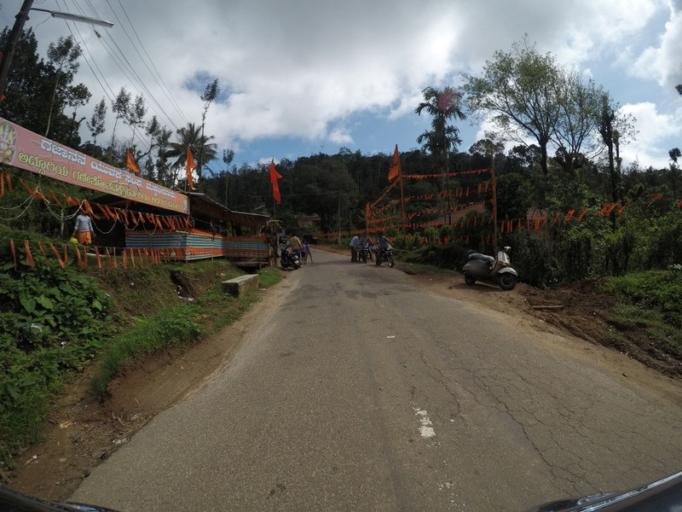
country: IN
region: Karnataka
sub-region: Kodagu
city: Madikeri
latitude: 12.4596
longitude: 75.7695
